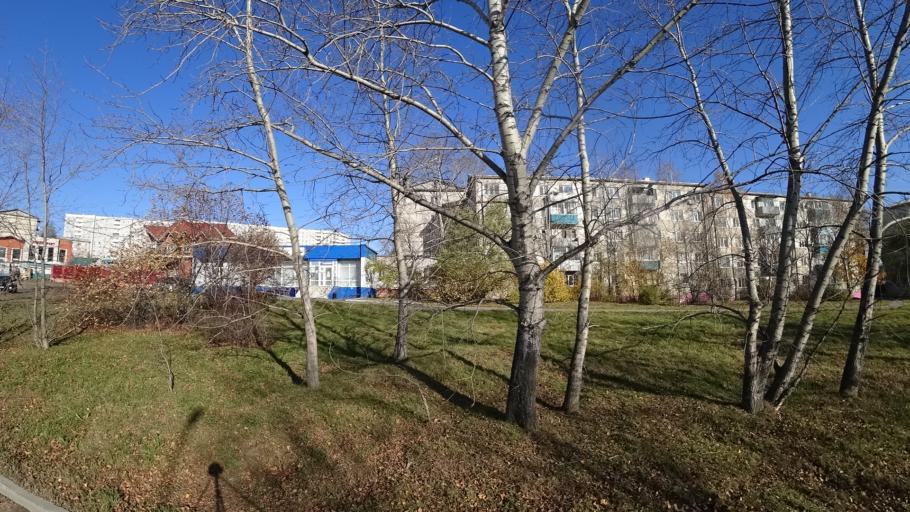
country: RU
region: Khabarovsk Krai
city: Amursk
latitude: 50.2367
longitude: 136.9111
